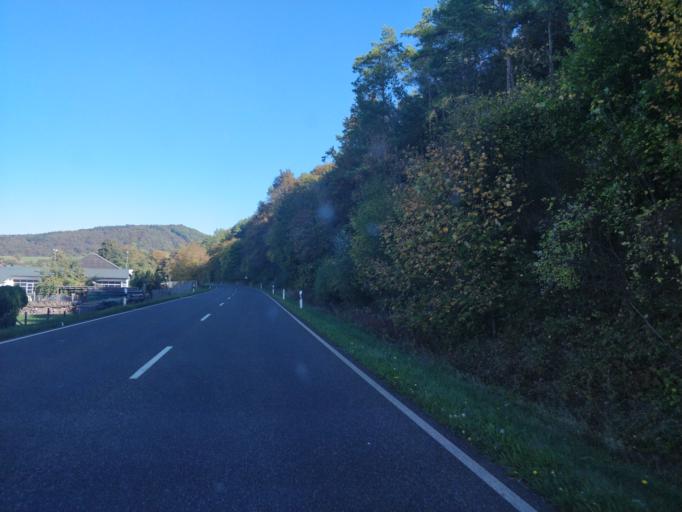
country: DE
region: North Rhine-Westphalia
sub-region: Regierungsbezirk Koln
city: Bad Munstereifel
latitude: 50.5475
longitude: 6.7125
